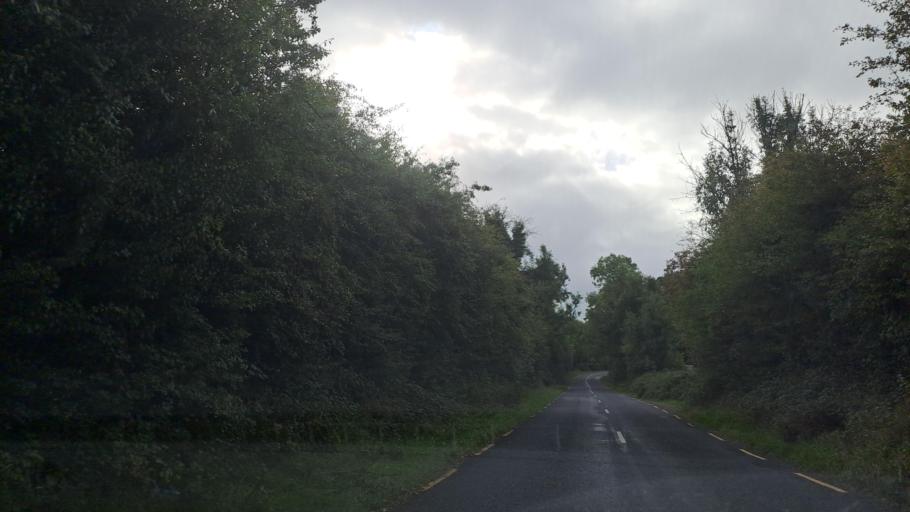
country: IE
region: Ulster
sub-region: County Monaghan
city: Carrickmacross
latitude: 54.0148
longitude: -6.7182
